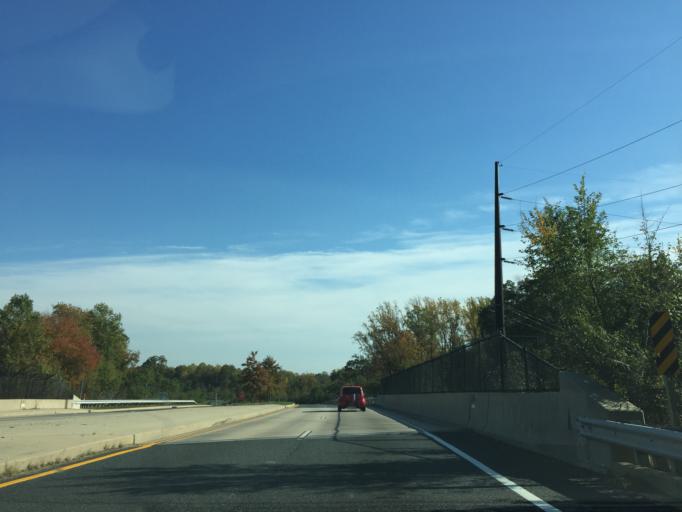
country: US
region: Maryland
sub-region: Baltimore County
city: White Marsh
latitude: 39.3632
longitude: -76.4246
